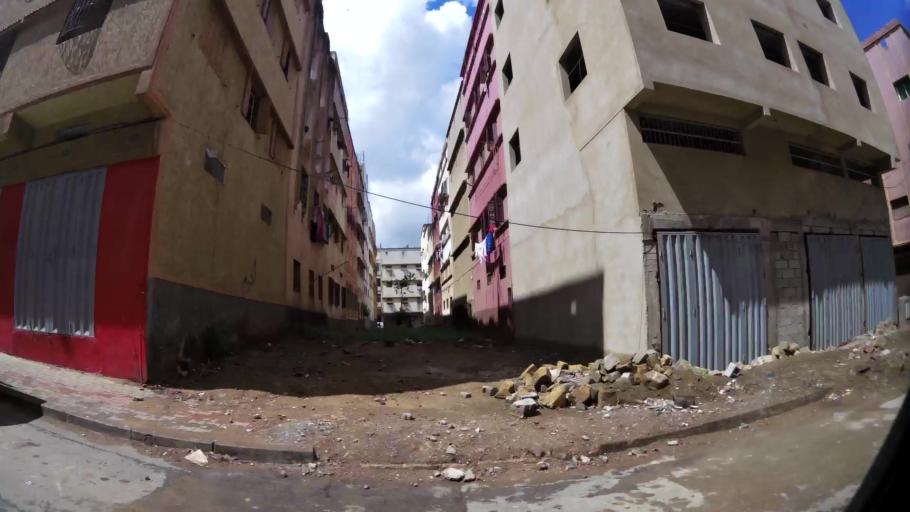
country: MA
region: Grand Casablanca
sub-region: Casablanca
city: Casablanca
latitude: 33.5370
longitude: -7.5667
